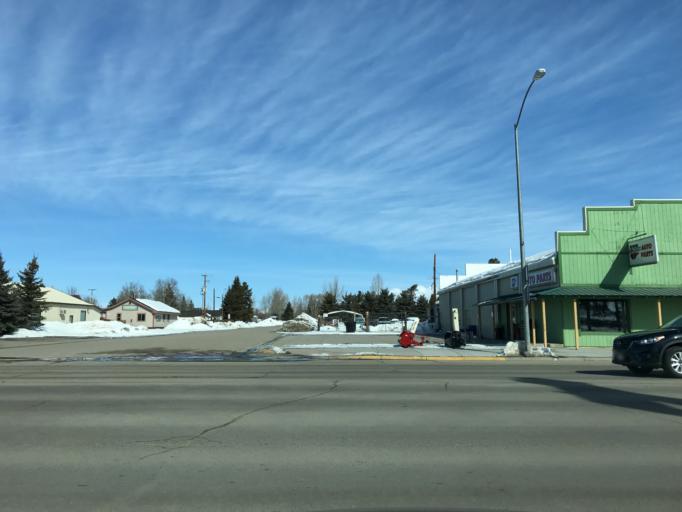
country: US
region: Wyoming
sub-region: Sublette County
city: Pinedale
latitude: 42.8664
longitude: -109.8698
